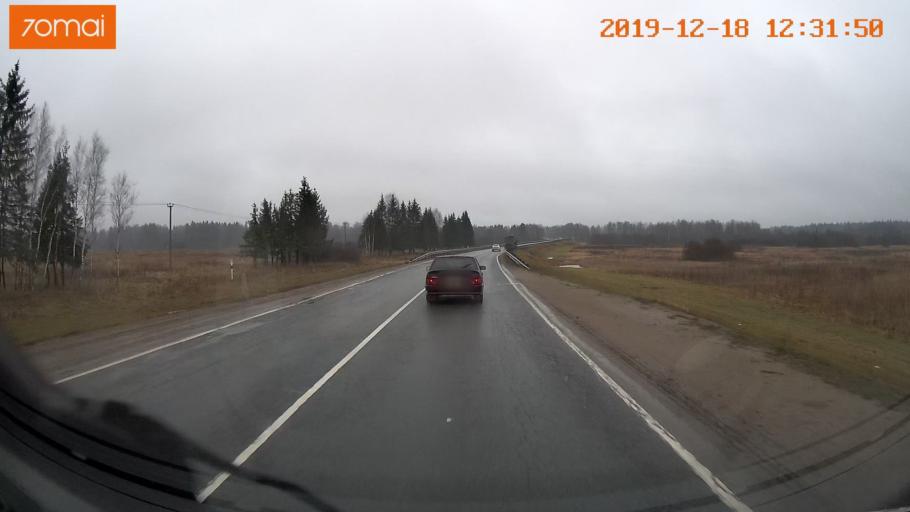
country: RU
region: Moskovskaya
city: Rumyantsevo
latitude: 56.1025
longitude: 36.5451
